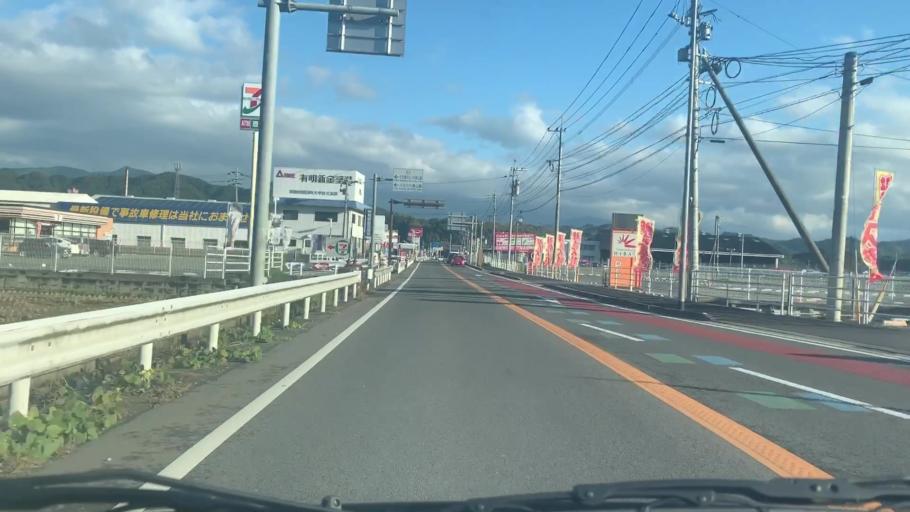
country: JP
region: Saga Prefecture
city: Takeocho-takeo
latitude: 33.2162
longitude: 130.0512
